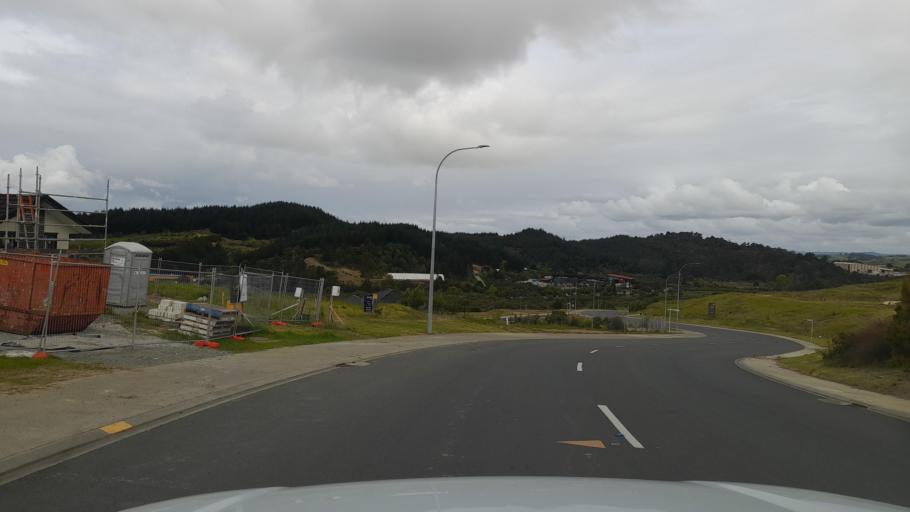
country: NZ
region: Northland
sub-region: Whangarei
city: Whangarei
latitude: -35.7437
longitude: 174.3173
